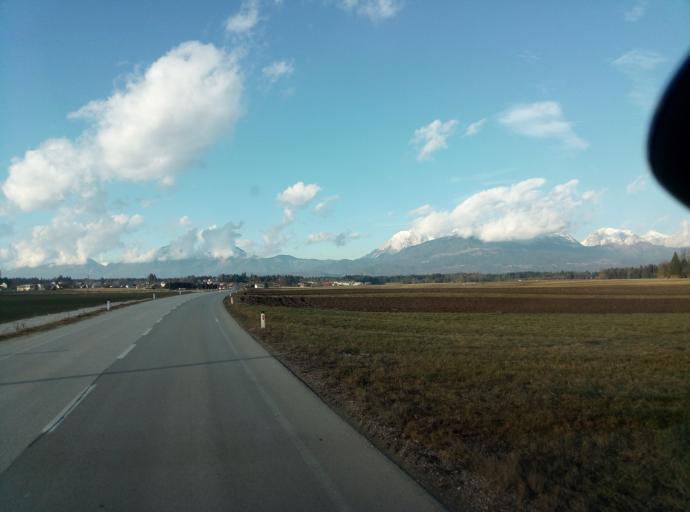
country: SI
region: Vodice
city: Vodice
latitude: 46.1781
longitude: 14.5037
